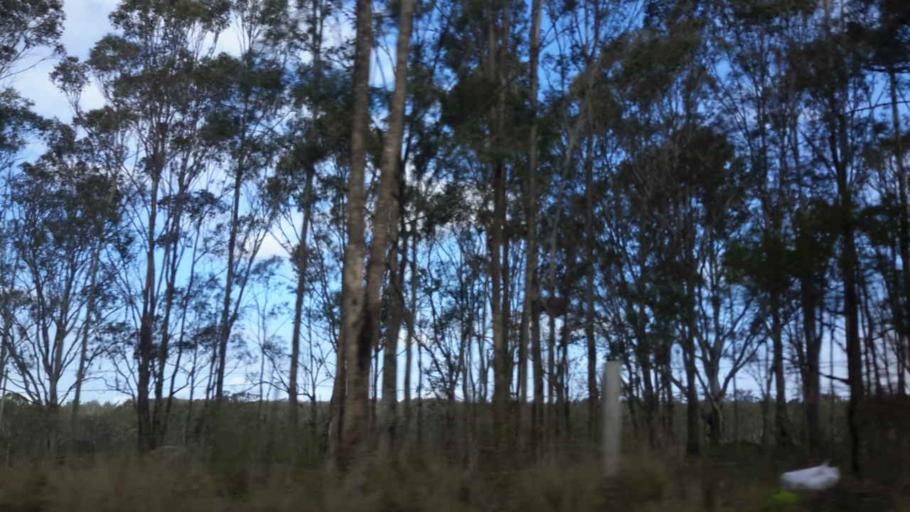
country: AU
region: New South Wales
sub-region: Campbelltown Municipality
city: Glen Alpine
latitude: -34.1226
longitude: 150.7948
